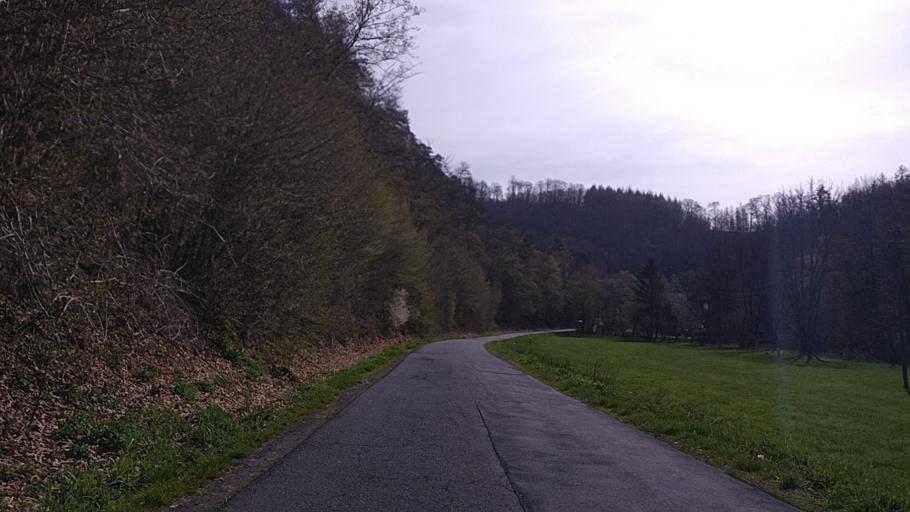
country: DE
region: Rheinland-Pfalz
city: Peterslahr
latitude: 50.6177
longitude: 7.4518
